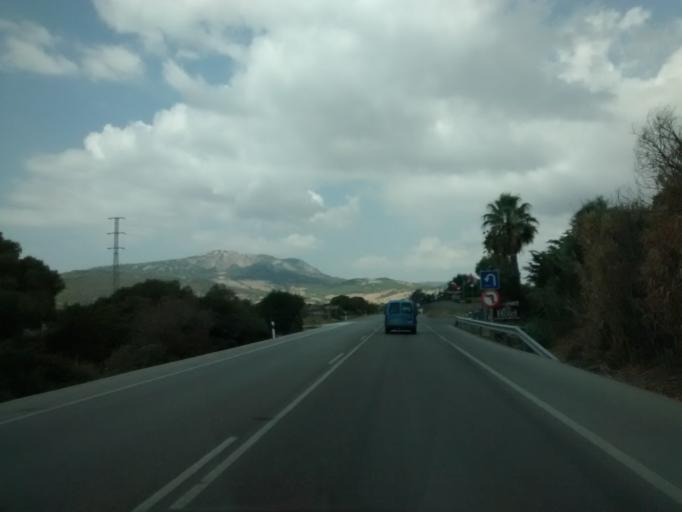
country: ES
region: Andalusia
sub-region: Provincia de Cadiz
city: Tarifa
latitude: 36.0668
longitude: -5.6778
